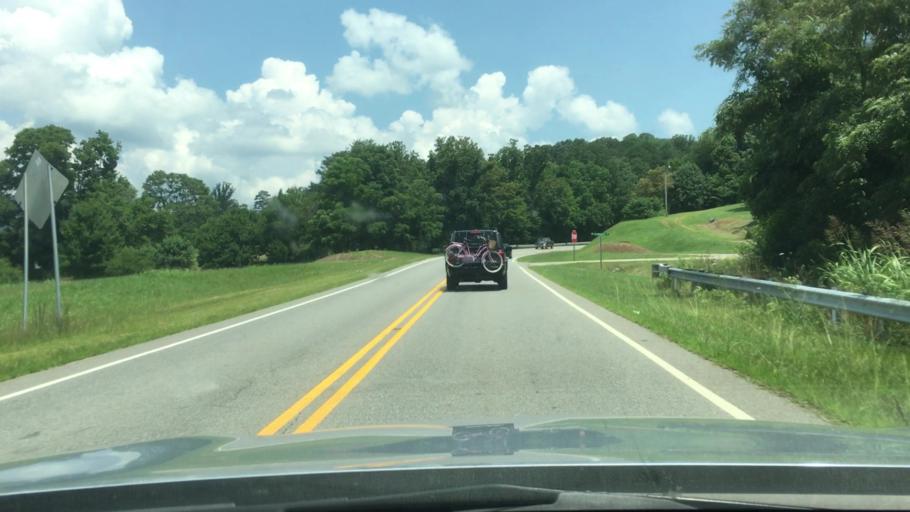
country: US
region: North Carolina
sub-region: Madison County
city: Marshall
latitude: 35.9055
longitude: -82.8708
